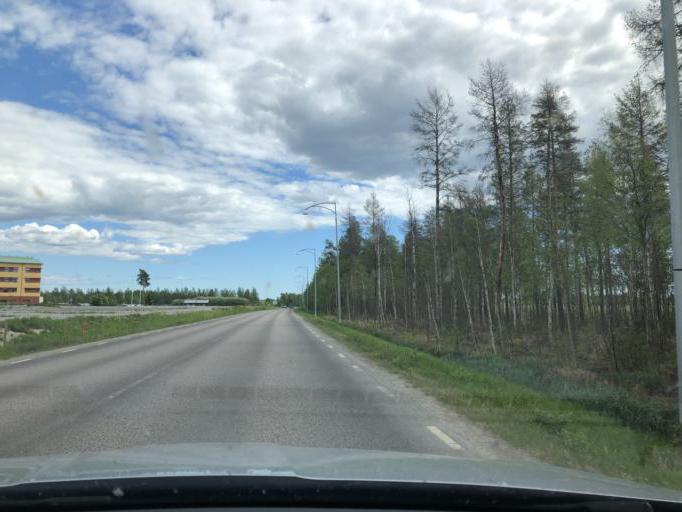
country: SE
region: Norrbotten
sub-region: Lulea Kommun
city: Sodra Sunderbyn
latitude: 65.6715
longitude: 21.9236
